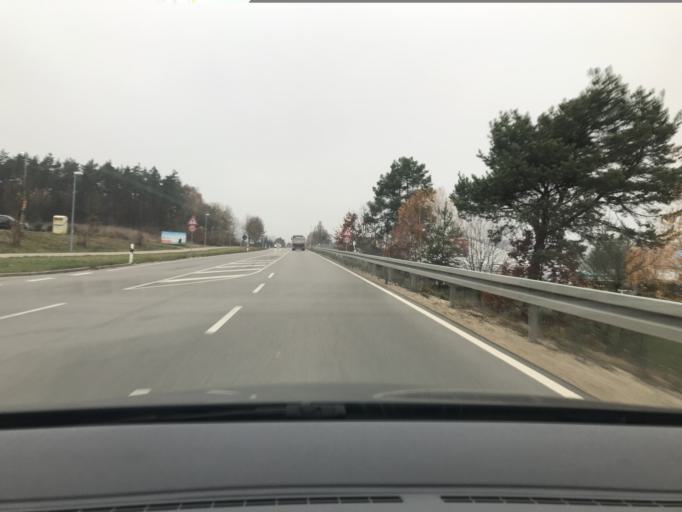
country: DE
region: Bavaria
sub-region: Regierungsbezirk Mittelfranken
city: Wilburgstetten
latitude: 49.0203
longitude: 10.3982
